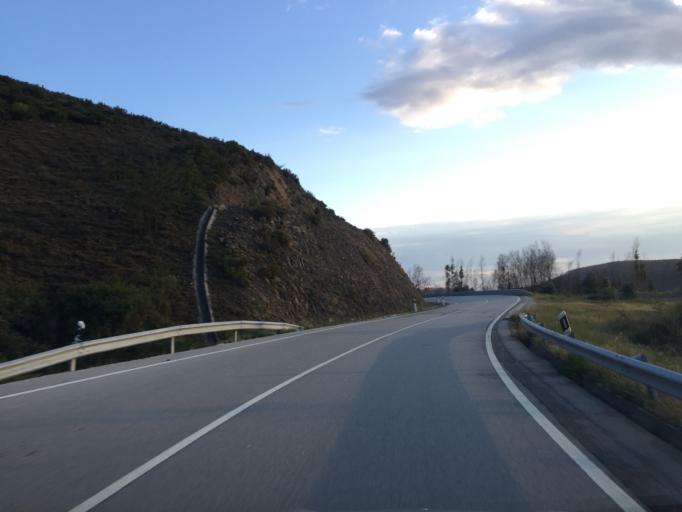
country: PT
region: Coimbra
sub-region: Pampilhosa da Serra
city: Pampilhosa da Serra
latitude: 40.0938
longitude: -7.9889
